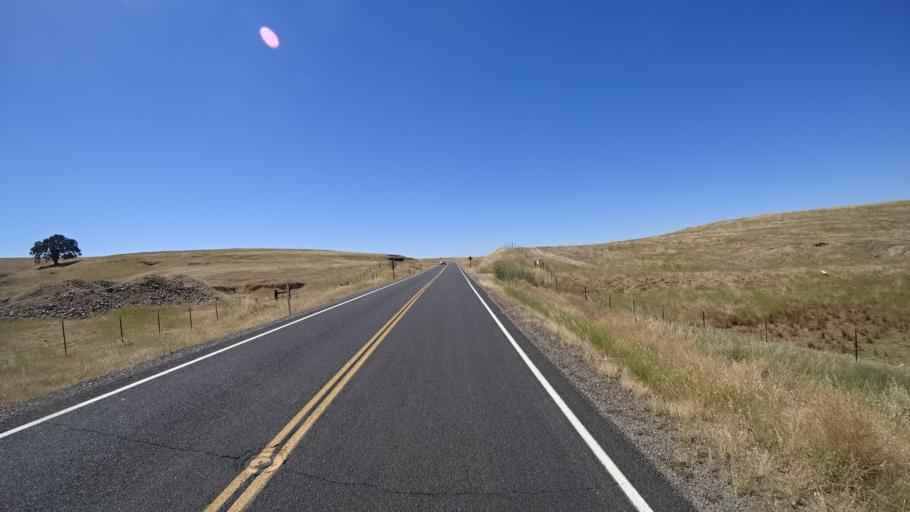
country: US
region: California
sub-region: Calaveras County
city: Rancho Calaveras
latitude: 38.0522
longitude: -120.8620
